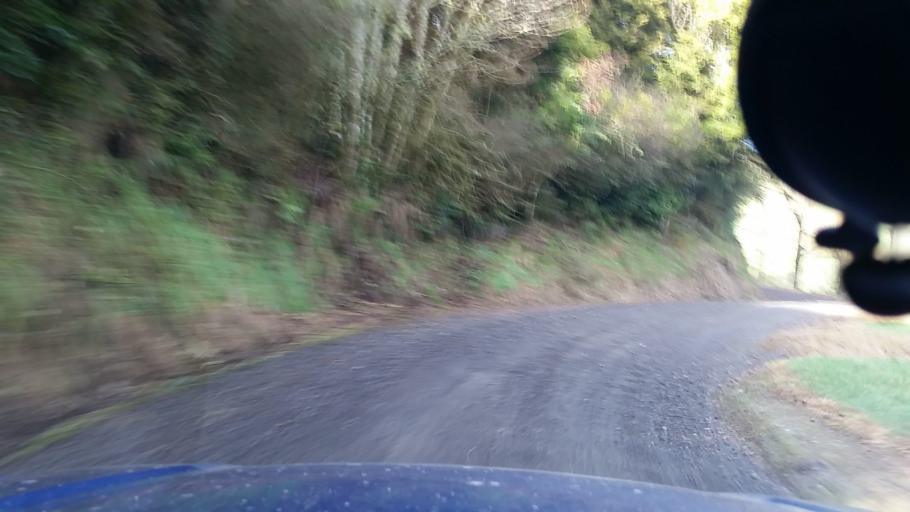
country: NZ
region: Taranaki
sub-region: New Plymouth District
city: Waitara
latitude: -39.0334
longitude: 174.7957
